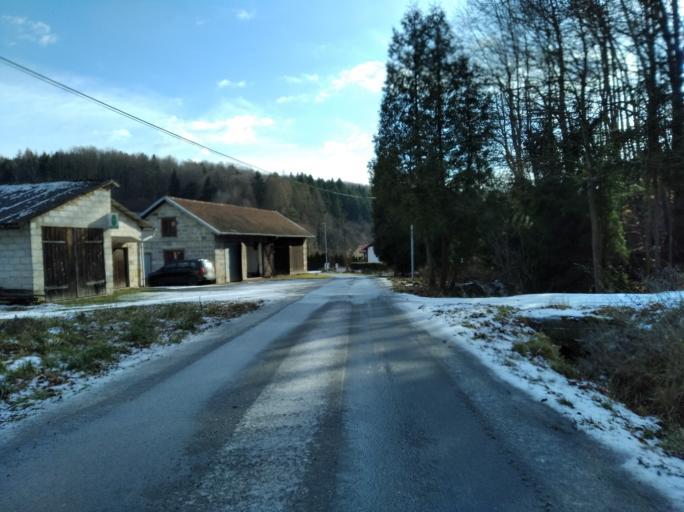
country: PL
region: Subcarpathian Voivodeship
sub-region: Powiat strzyzowski
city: Strzyzow
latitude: 49.8961
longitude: 21.7747
